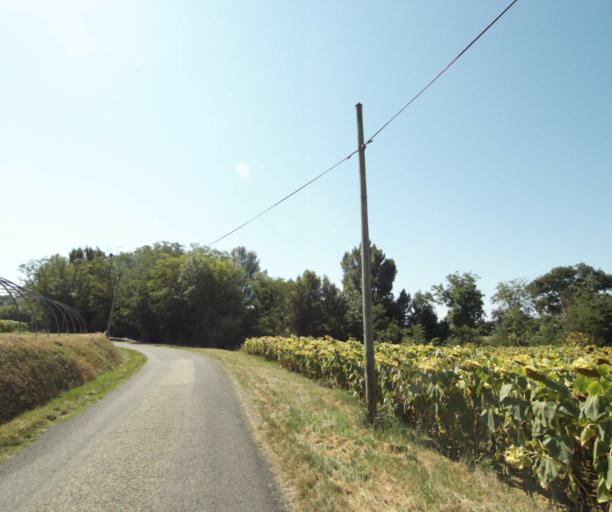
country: FR
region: Midi-Pyrenees
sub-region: Departement de l'Ariege
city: Lezat-sur-Leze
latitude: 43.2704
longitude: 1.3590
